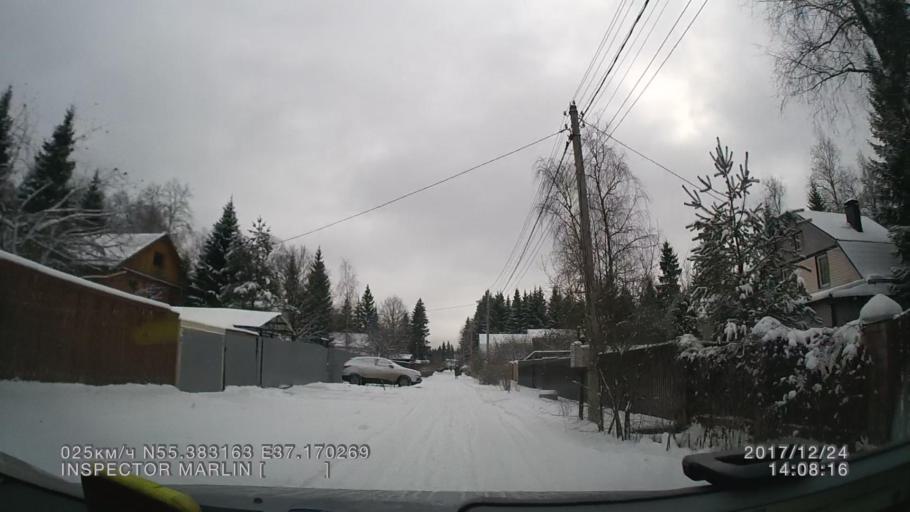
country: RU
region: Moskovskaya
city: Troitsk
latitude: 55.3831
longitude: 37.1705
